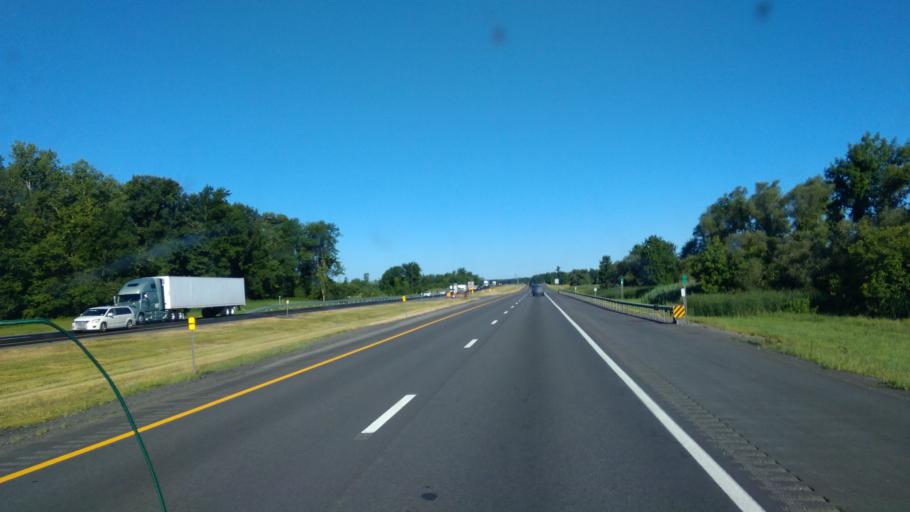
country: US
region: New York
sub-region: Ontario County
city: Victor
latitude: 42.9921
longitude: -77.3310
